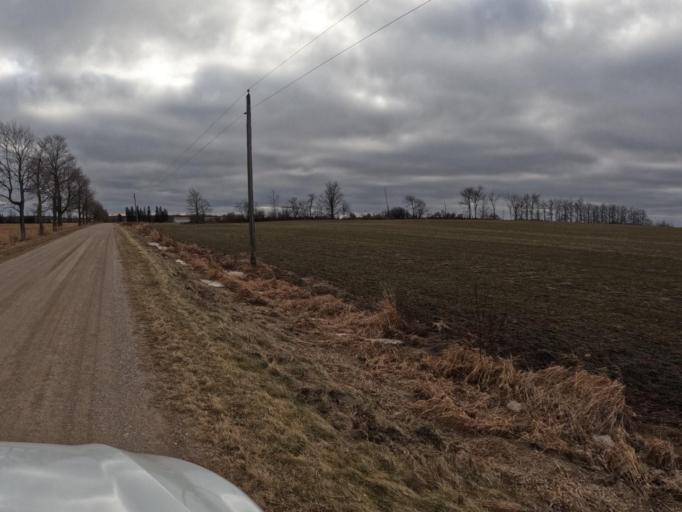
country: CA
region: Ontario
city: Shelburne
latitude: 43.8939
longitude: -80.3297
